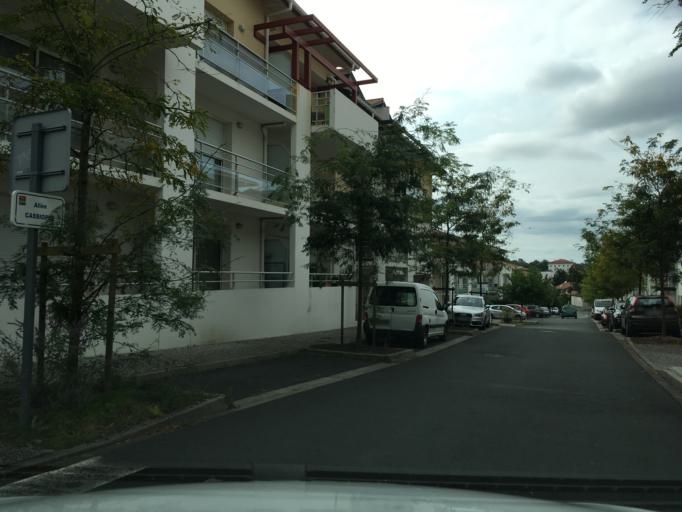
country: FR
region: Aquitaine
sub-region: Departement des Pyrenees-Atlantiques
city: Anglet
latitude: 43.4956
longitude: -1.5111
